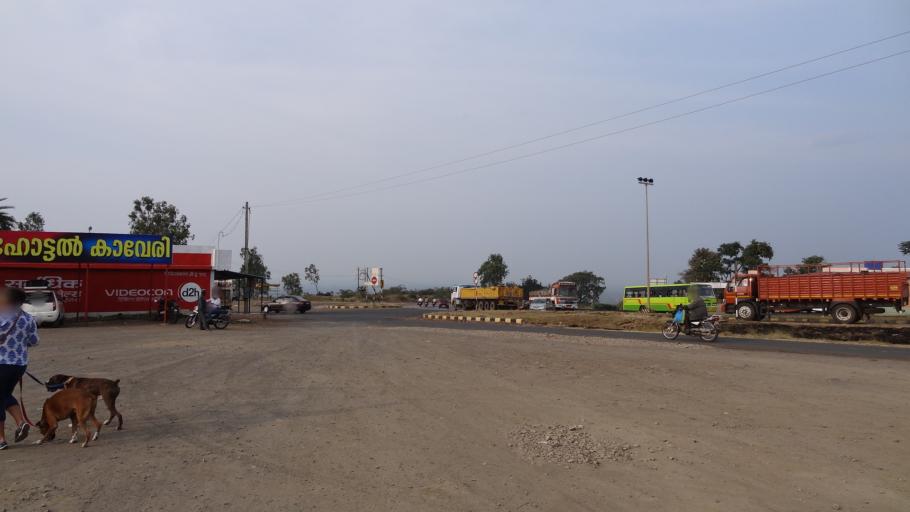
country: IN
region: Maharashtra
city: Nipani
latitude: 16.3478
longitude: 74.3941
